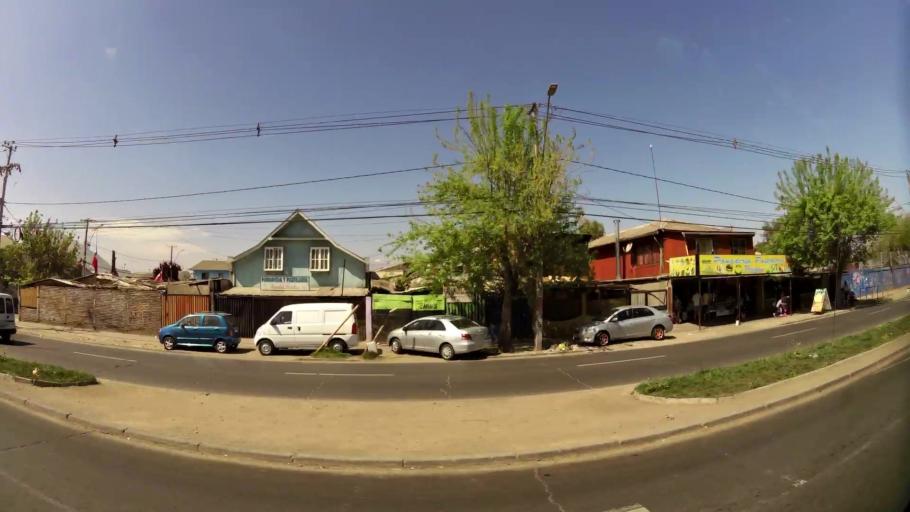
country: CL
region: Santiago Metropolitan
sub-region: Provincia de Santiago
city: Lo Prado
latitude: -33.4046
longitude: -70.7451
